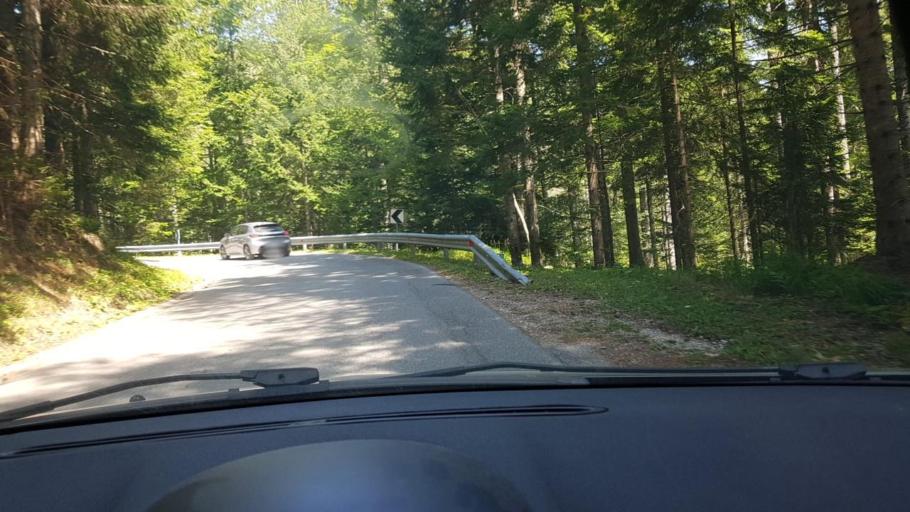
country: AT
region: Carinthia
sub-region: Politischer Bezirk Volkermarkt
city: Bad Eisenkappel
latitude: 46.4269
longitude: 14.5997
